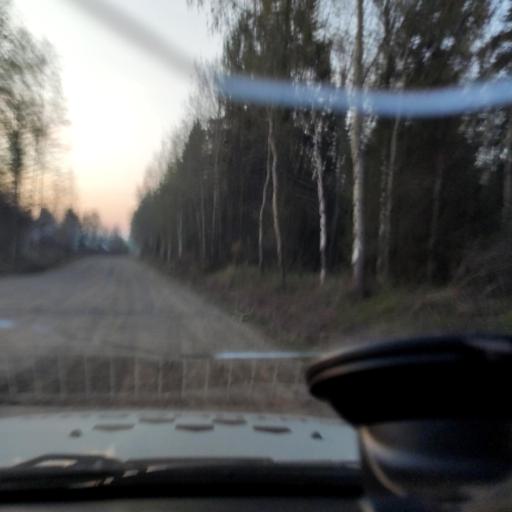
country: RU
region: Perm
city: Yug
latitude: 57.5887
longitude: 56.2046
